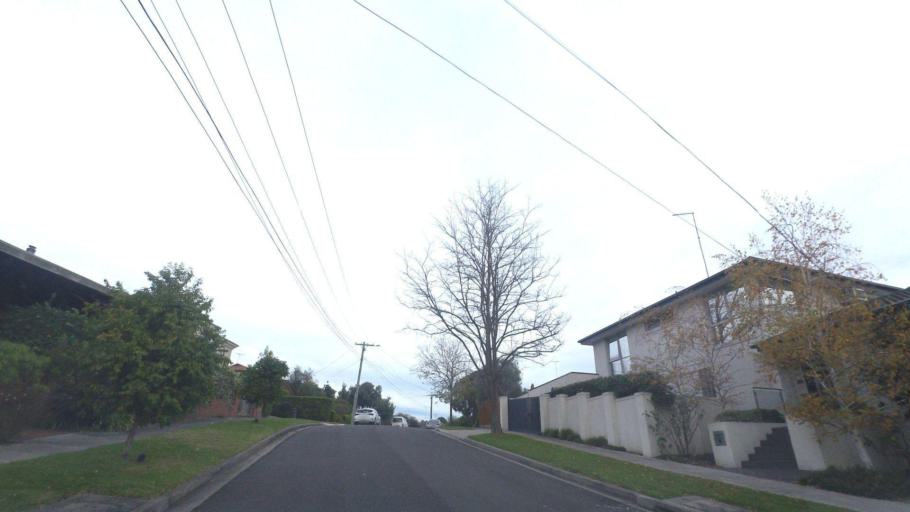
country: AU
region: Victoria
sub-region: Manningham
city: Bulleen
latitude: -37.7729
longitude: 145.0878
